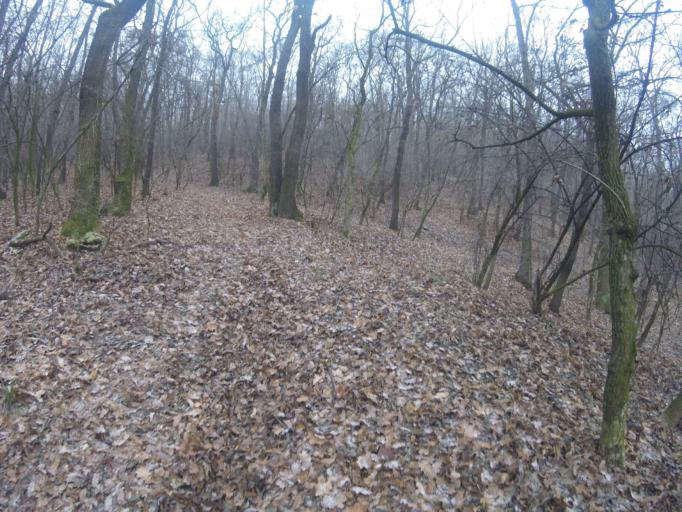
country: HU
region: Fejer
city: Bicske
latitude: 47.4184
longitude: 18.5786
